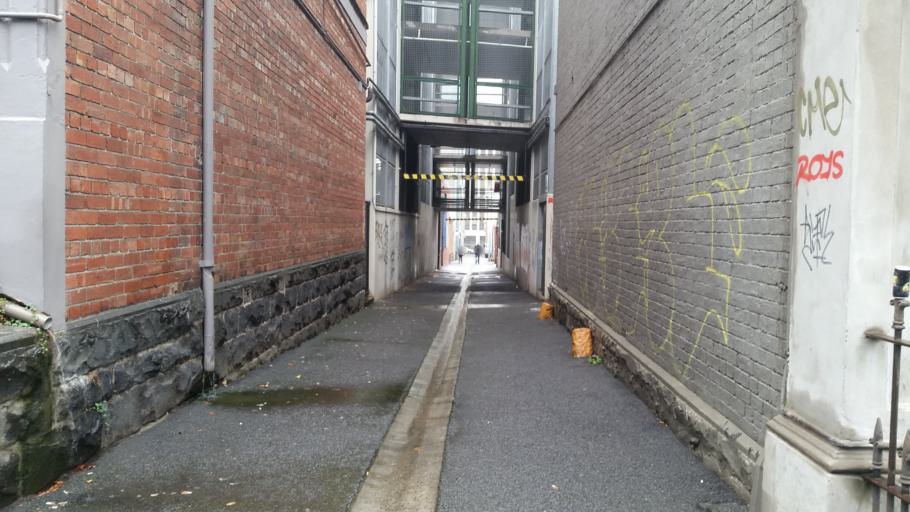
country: AU
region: Victoria
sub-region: Yarra
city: Fitzroy
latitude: -37.8090
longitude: 144.9767
